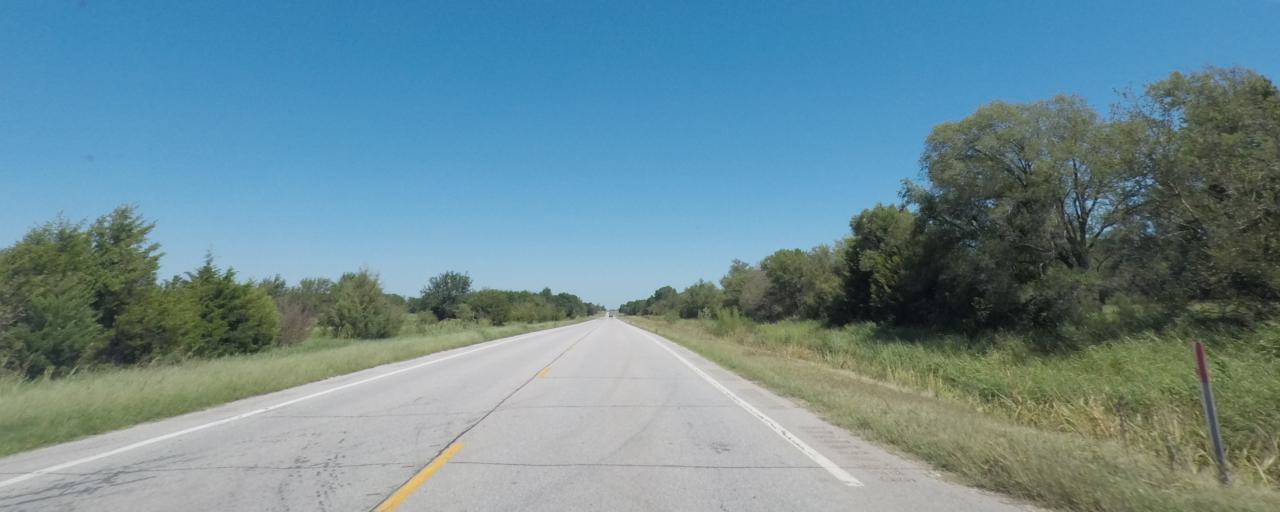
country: US
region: Kansas
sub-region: Sumner County
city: Belle Plaine
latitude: 37.3765
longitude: -97.3850
